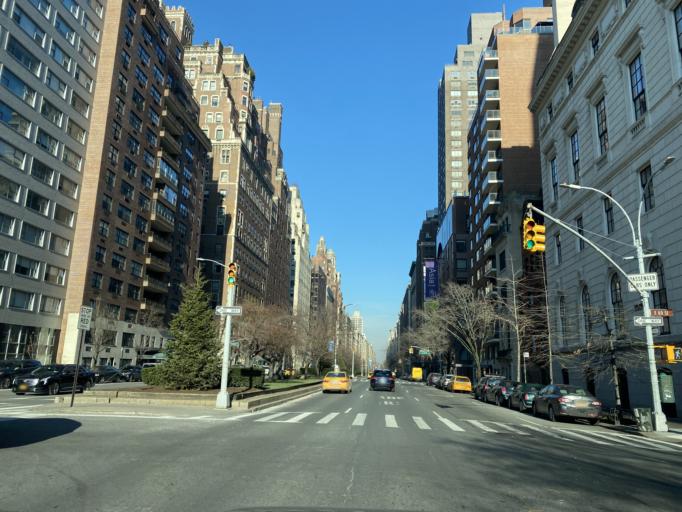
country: US
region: New York
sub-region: New York County
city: Manhattan
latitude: 40.7691
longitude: -73.9653
